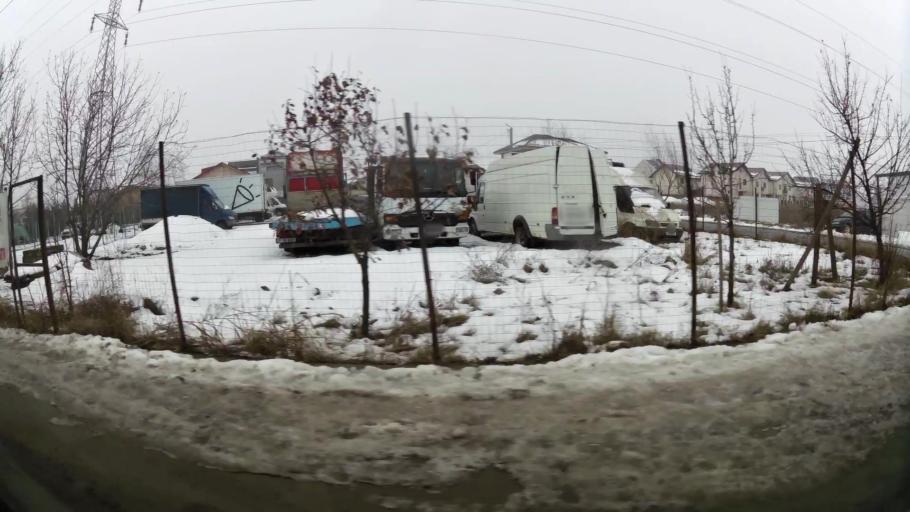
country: RO
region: Ilfov
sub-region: Comuna Chiajna
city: Rosu
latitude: 44.4474
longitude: 25.9961
